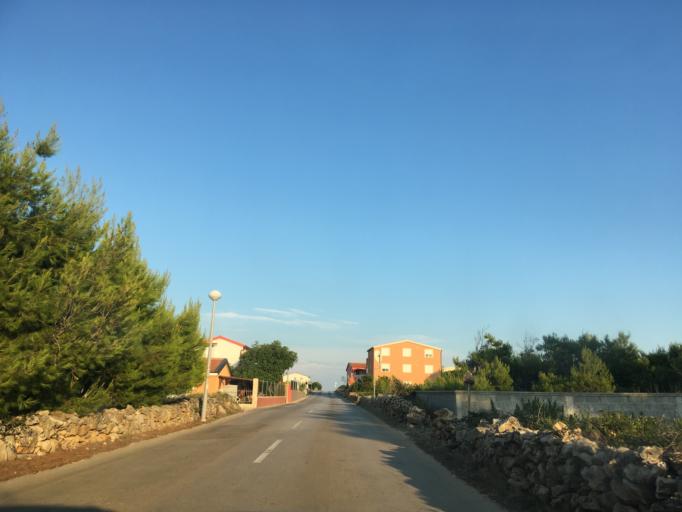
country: HR
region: Zadarska
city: Vir
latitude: 44.2998
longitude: 15.1119
